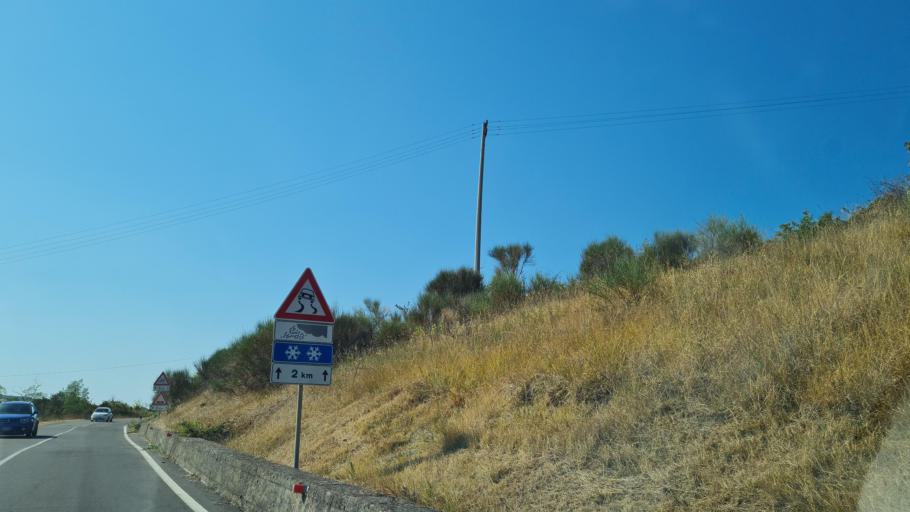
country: IT
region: Tuscany
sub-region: Provincia di Siena
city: Abbadia San Salvatore
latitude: 42.9394
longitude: 11.7114
